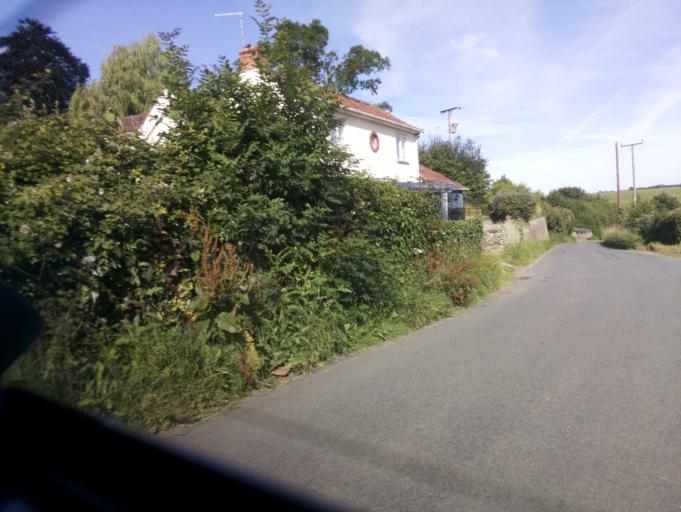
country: GB
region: England
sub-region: South Gloucestershire
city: Bitton
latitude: 51.4384
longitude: -2.4356
